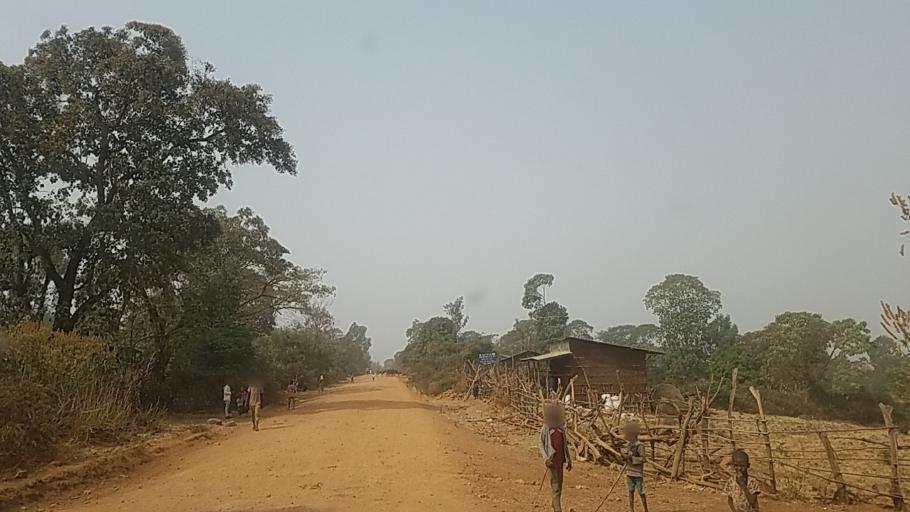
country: ET
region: Amhara
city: Bure
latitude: 10.7894
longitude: 36.3057
